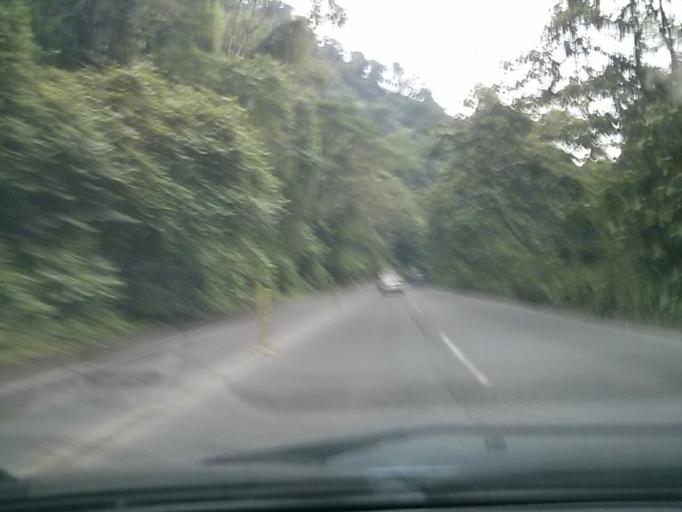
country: CR
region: San Jose
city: Dulce Nombre de Jesus
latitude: 10.1503
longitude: -83.9562
